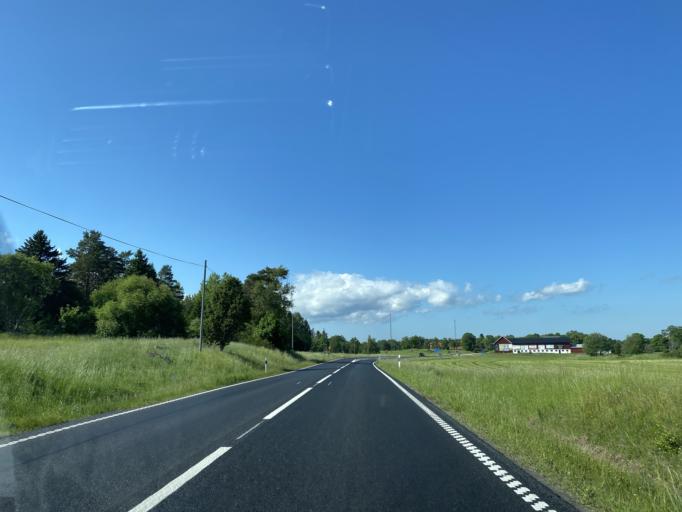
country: SE
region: Stockholm
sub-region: Norrtalje Kommun
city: Norrtalje
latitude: 59.8788
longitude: 18.6993
